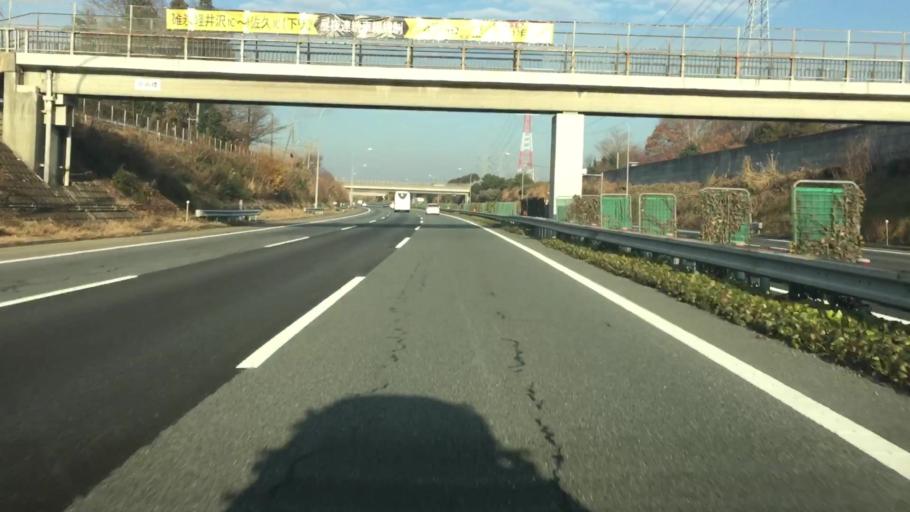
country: JP
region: Saitama
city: Sakado
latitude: 36.0364
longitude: 139.3766
